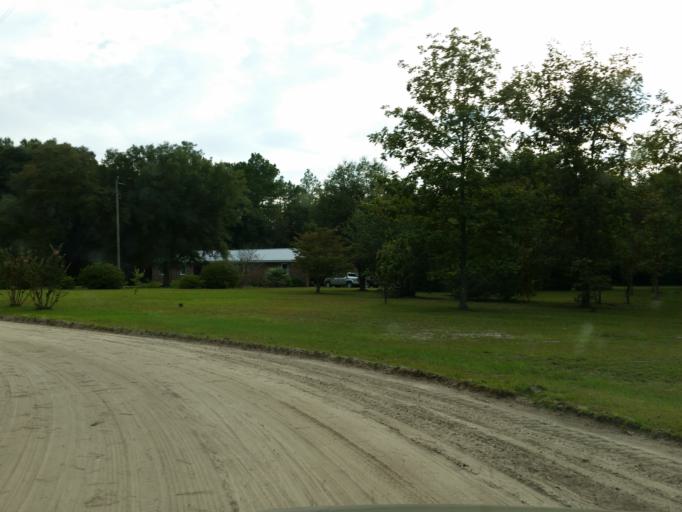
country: US
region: Florida
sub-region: Madison County
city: Madison
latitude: 30.5192
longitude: -83.2199
